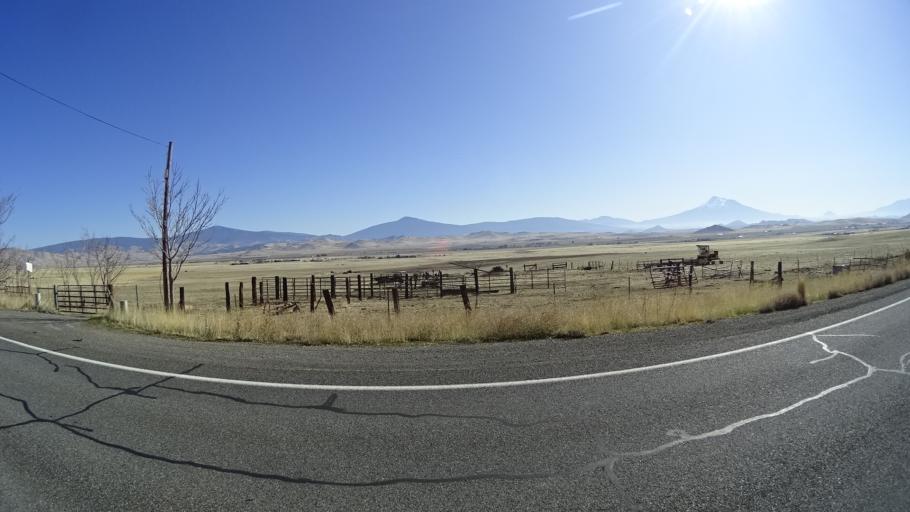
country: US
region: California
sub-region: Siskiyou County
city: Montague
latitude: 41.7849
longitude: -122.5183
